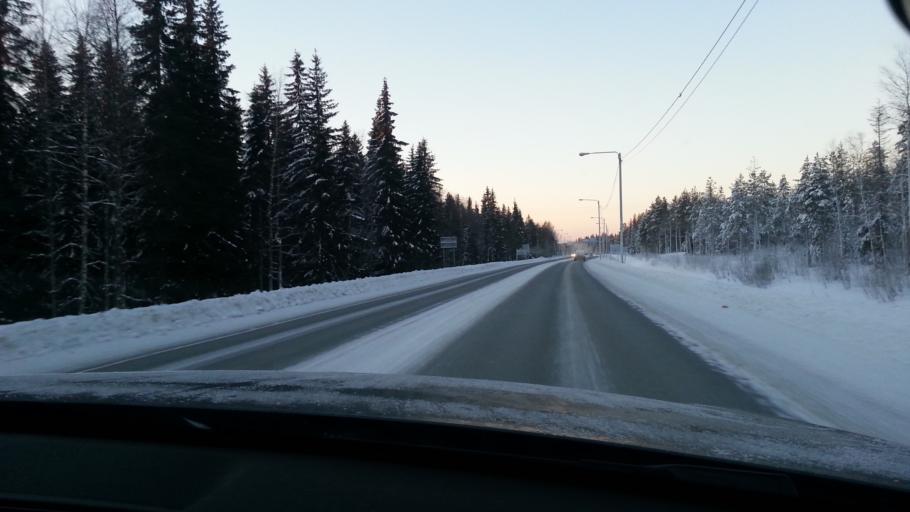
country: FI
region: Lapland
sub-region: Rovaniemi
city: Rovaniemi
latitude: 66.5428
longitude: 25.8285
